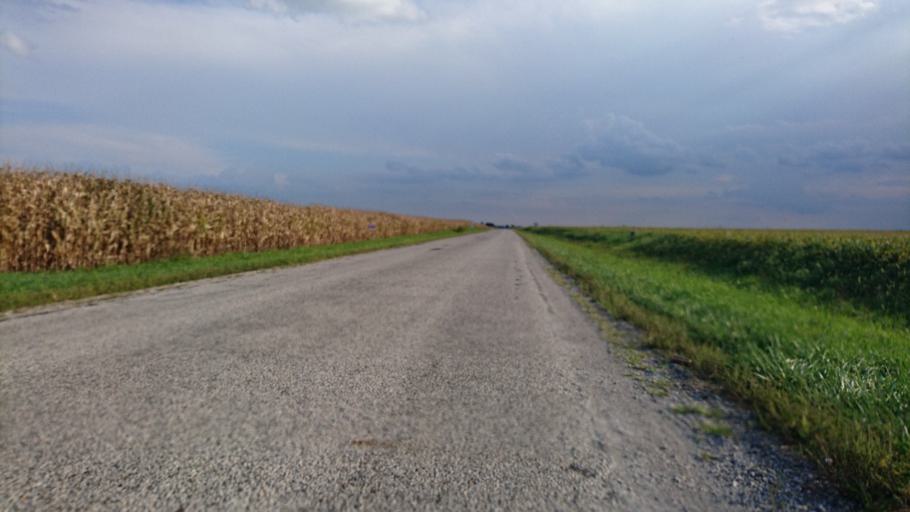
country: US
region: Illinois
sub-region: Logan County
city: Atlanta
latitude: 40.2578
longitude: -89.2053
